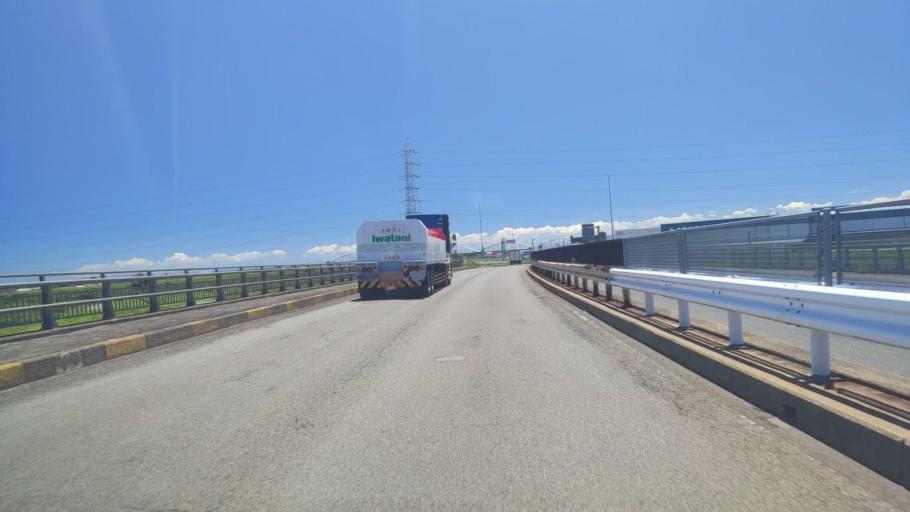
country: JP
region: Mie
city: Yokkaichi
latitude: 34.9245
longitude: 136.6150
